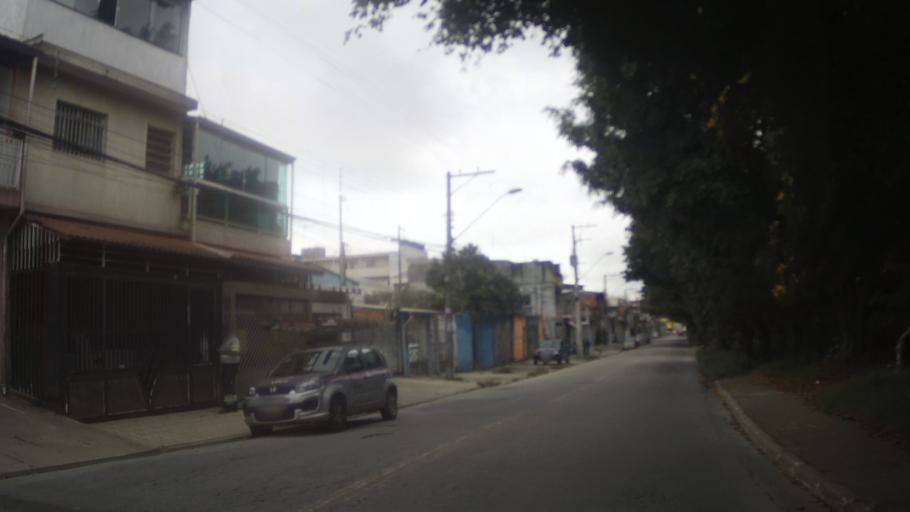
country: BR
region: Sao Paulo
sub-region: Guarulhos
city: Guarulhos
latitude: -23.4225
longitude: -46.5297
